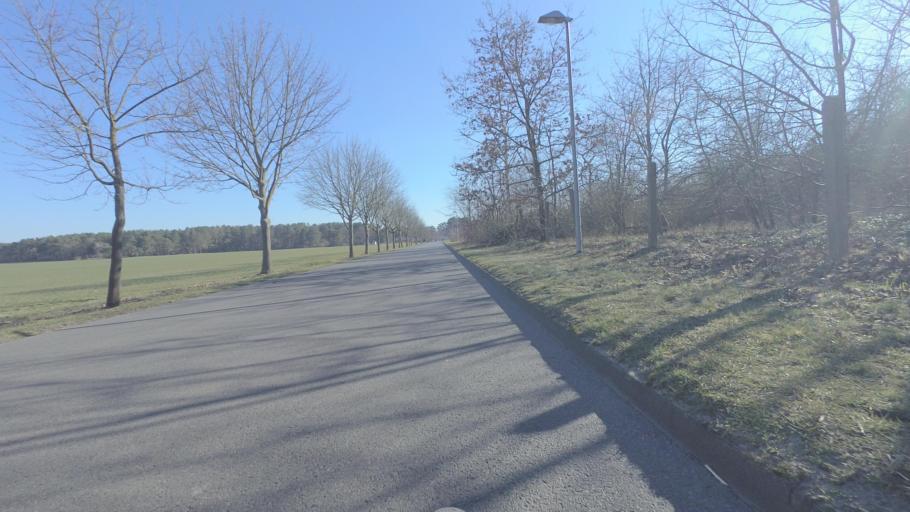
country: DE
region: Brandenburg
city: Rangsdorf
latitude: 52.2519
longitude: 13.4214
